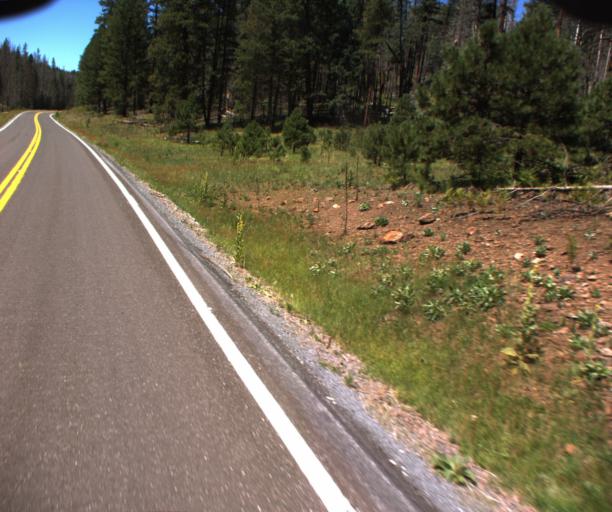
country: US
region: Arizona
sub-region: Apache County
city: Eagar
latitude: 33.6467
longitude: -109.3125
